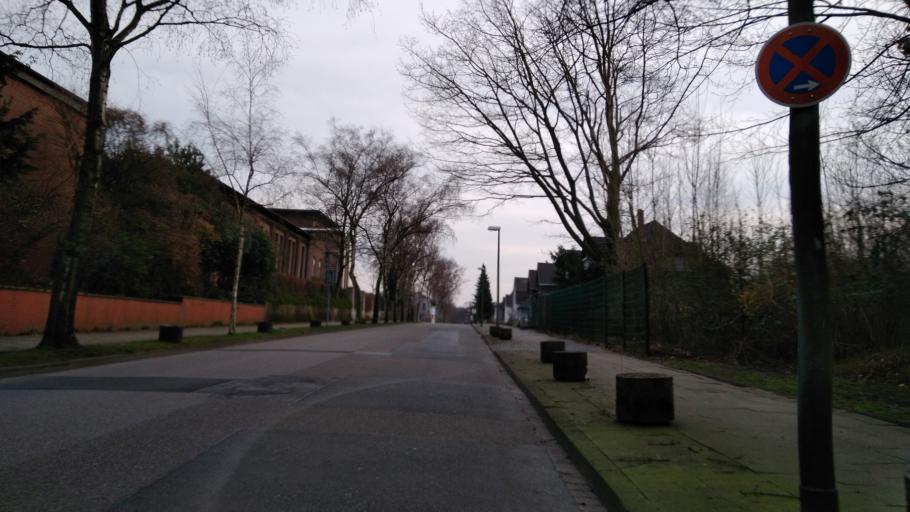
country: DE
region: North Rhine-Westphalia
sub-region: Regierungsbezirk Munster
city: Gladbeck
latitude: 51.5964
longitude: 7.0416
